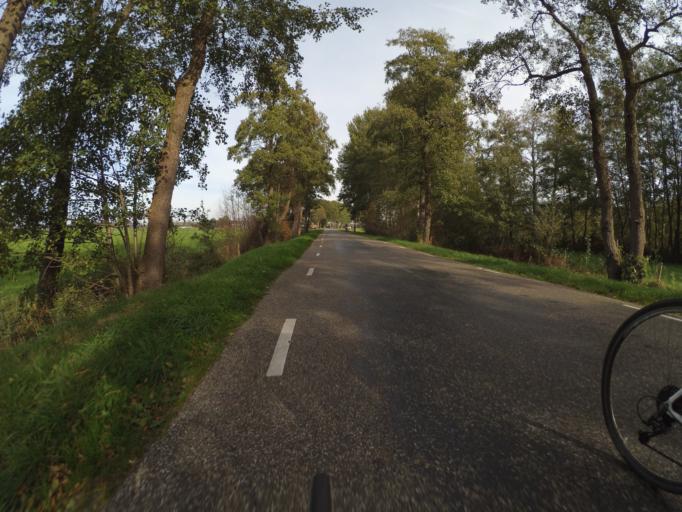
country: NL
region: Gelderland
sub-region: Gemeente Lochem
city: Laren
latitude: 52.2522
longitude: 6.3948
